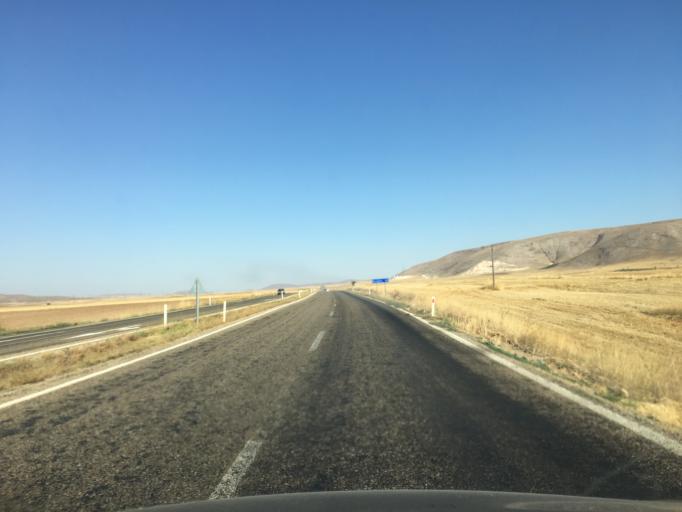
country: TR
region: Kirsehir
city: Akpinar
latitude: 39.3431
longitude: 33.9642
